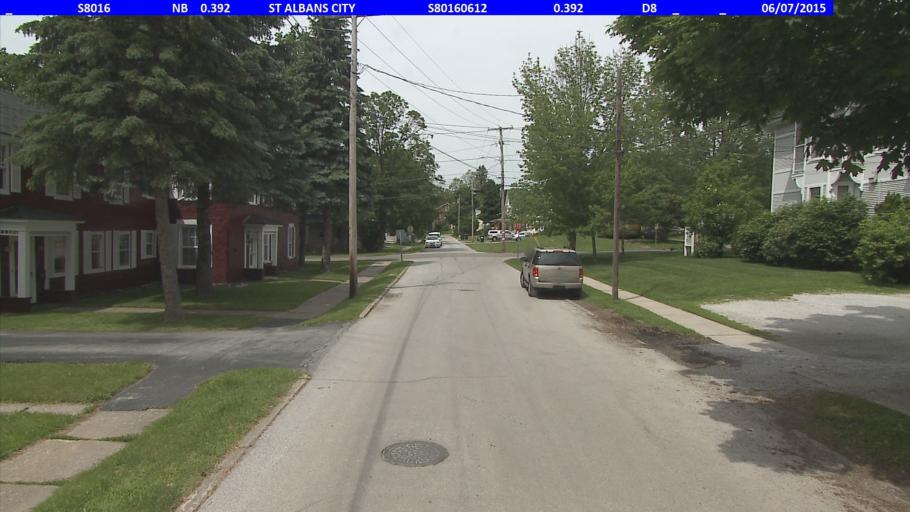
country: US
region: Vermont
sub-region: Franklin County
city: Saint Albans
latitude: 44.8117
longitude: -73.0802
